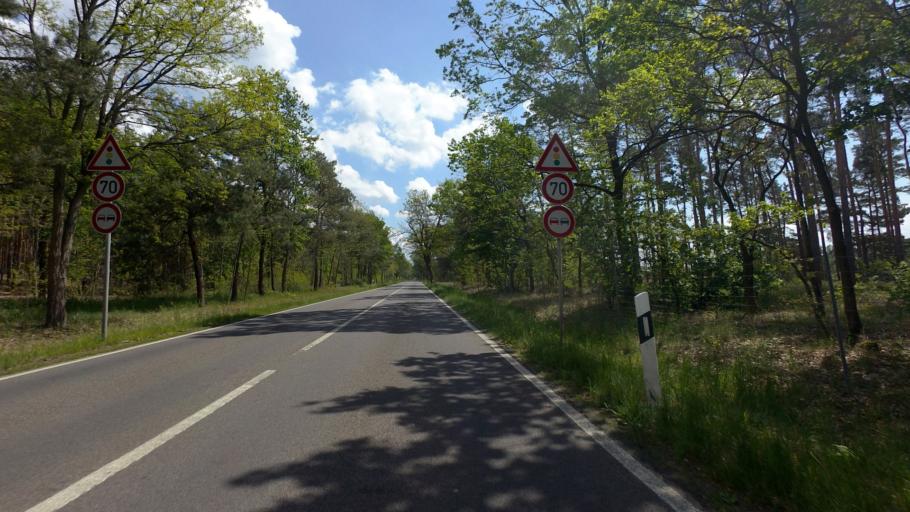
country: DE
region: Brandenburg
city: Luebben
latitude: 51.9447
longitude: 13.9636
